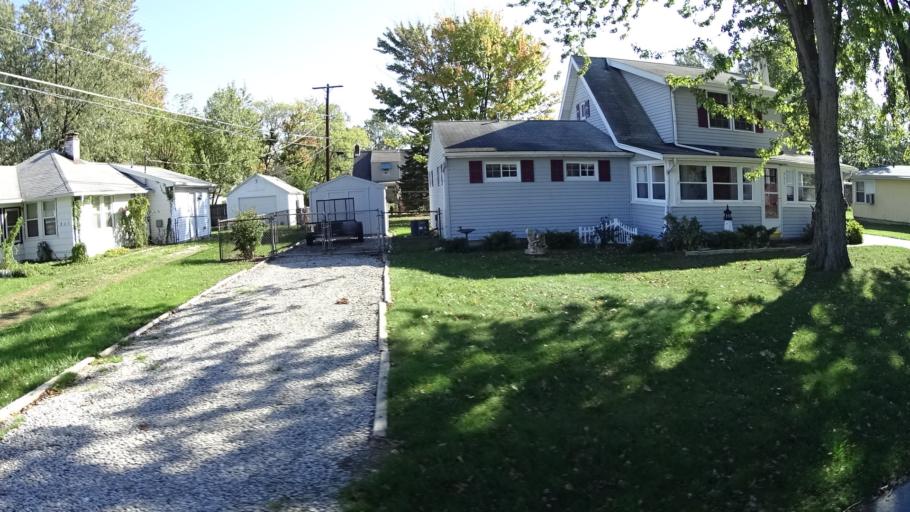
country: US
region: Ohio
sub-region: Lorain County
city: Vermilion-on-the-Lake
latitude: 41.4271
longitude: -82.3394
